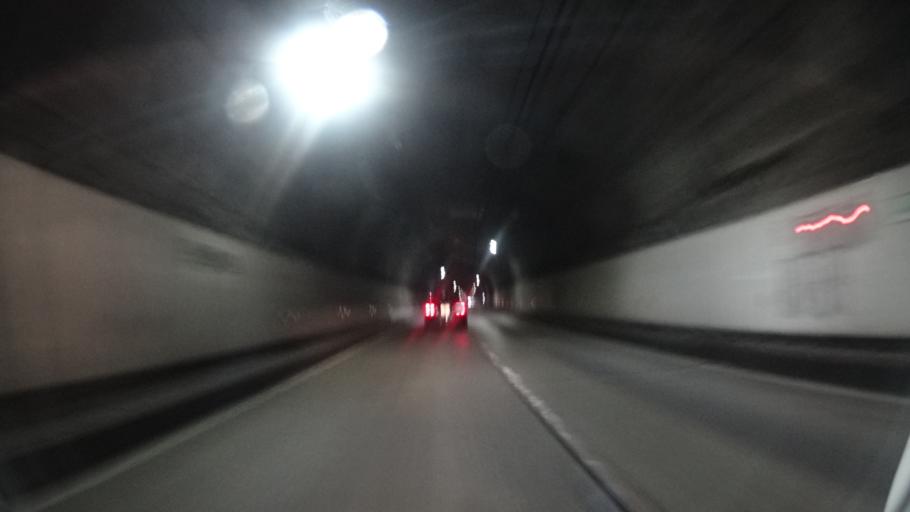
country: JP
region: Ehime
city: Kawanoecho
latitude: 33.9968
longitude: 133.6860
